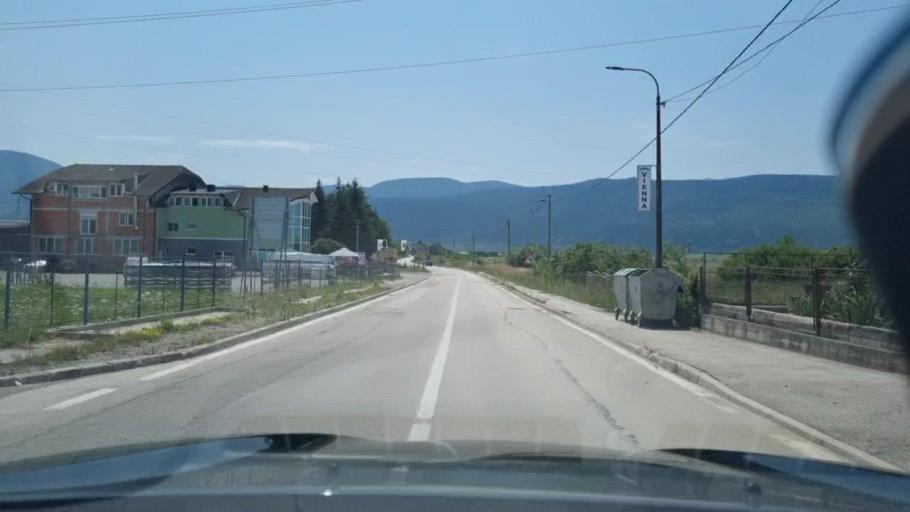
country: BA
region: Federation of Bosnia and Herzegovina
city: Sanica
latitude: 44.5436
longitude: 16.3629
